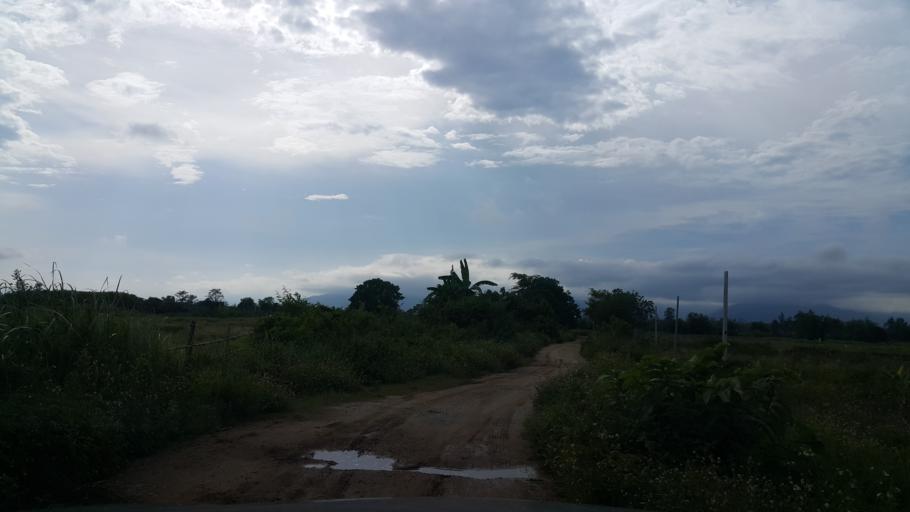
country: TH
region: Chiang Rai
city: Wiang Chai
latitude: 19.9727
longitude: 99.9169
